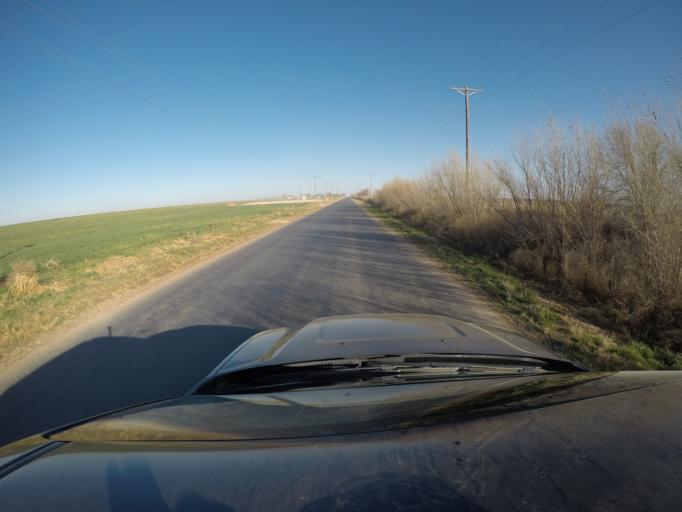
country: US
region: New Mexico
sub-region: Curry County
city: Texico
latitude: 34.3029
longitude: -103.1338
